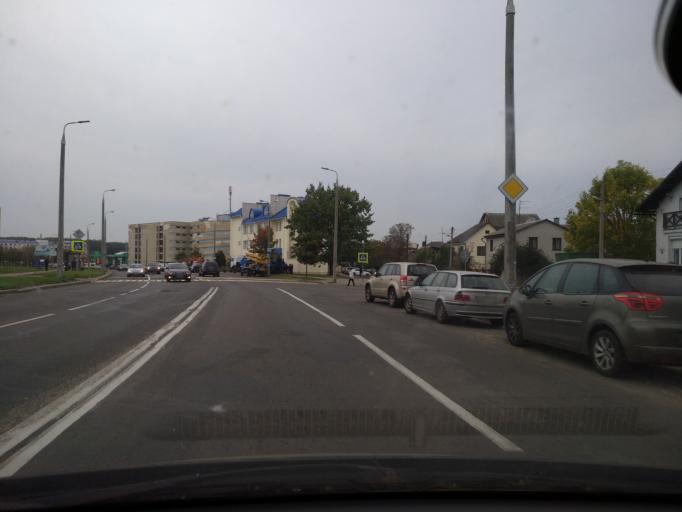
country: BY
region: Minsk
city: Minsk
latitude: 53.9388
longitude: 27.5758
